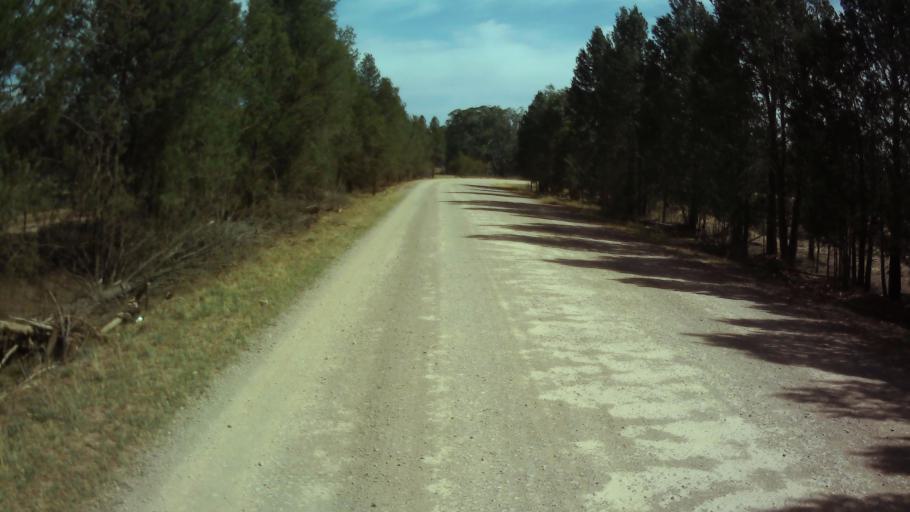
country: AU
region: New South Wales
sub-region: Weddin
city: Grenfell
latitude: -34.0386
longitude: 148.0806
